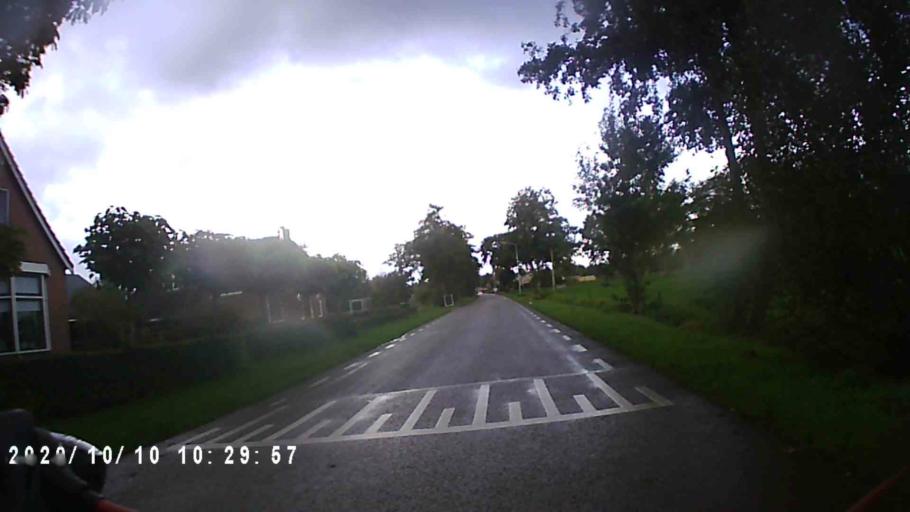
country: NL
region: Groningen
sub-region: Gemeente Leek
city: Leek
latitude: 53.1872
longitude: 6.3357
